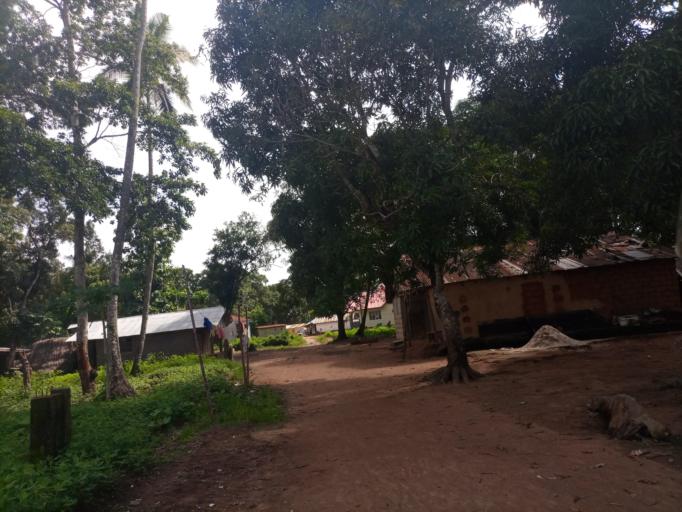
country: SL
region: Northern Province
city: Sawkta
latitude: 8.6310
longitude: -13.1836
